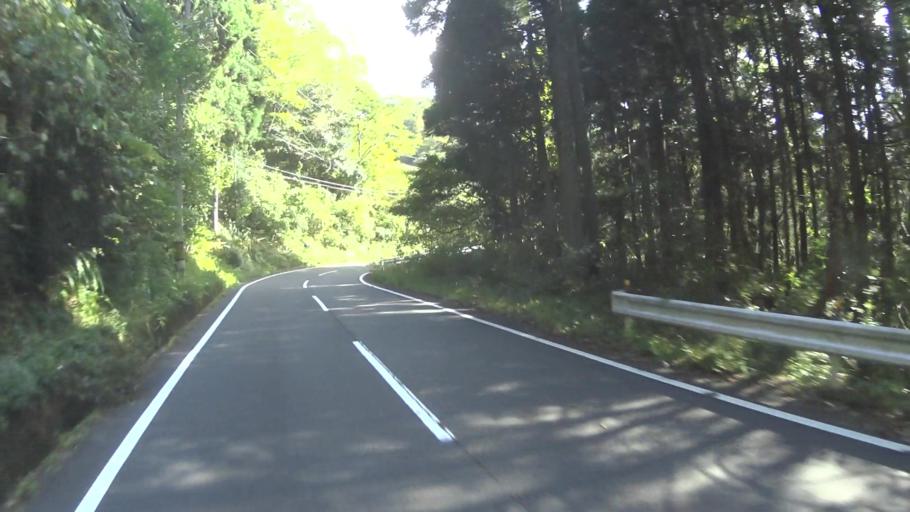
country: JP
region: Kyoto
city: Maizuru
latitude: 35.5364
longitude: 135.4437
